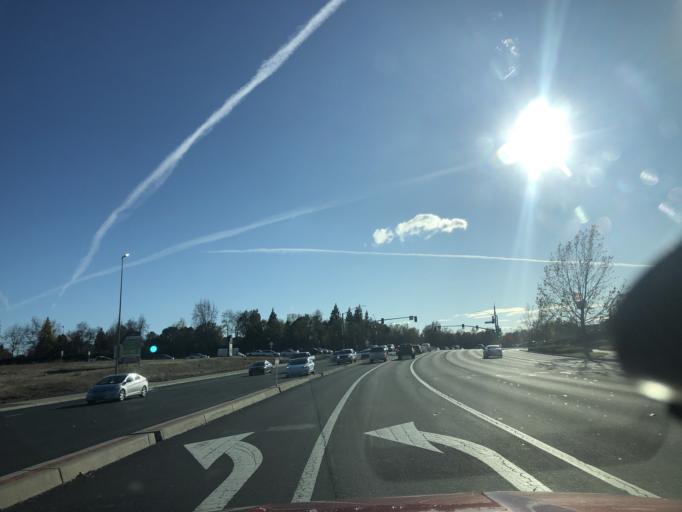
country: US
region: California
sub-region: Placer County
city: Roseville
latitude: 38.7796
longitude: -121.2875
